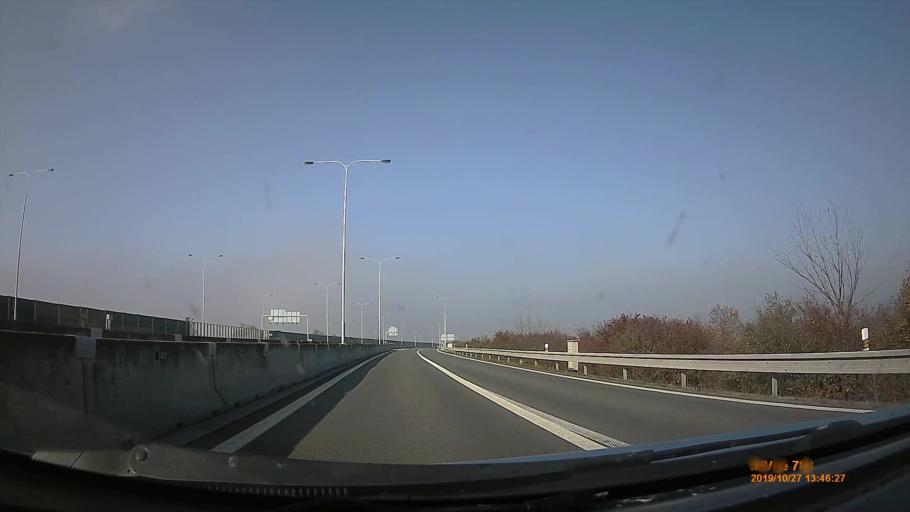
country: CZ
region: Olomoucky
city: Hnevotin
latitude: 49.5726
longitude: 17.2121
